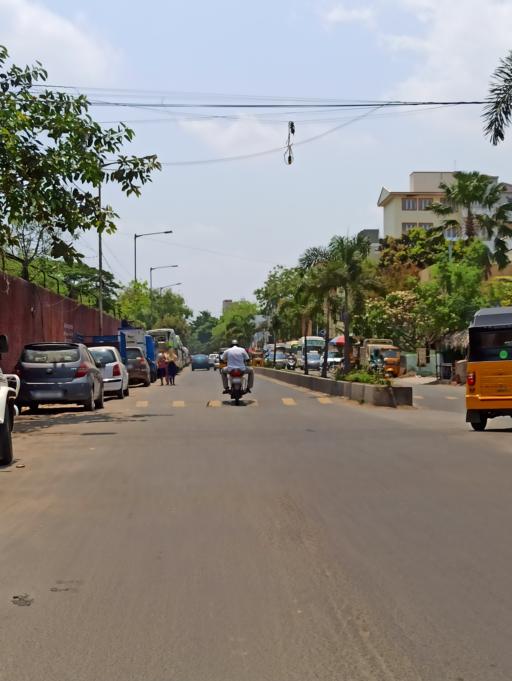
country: IN
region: Tamil Nadu
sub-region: Chennai
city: Chetput
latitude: 13.0928
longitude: 80.2364
